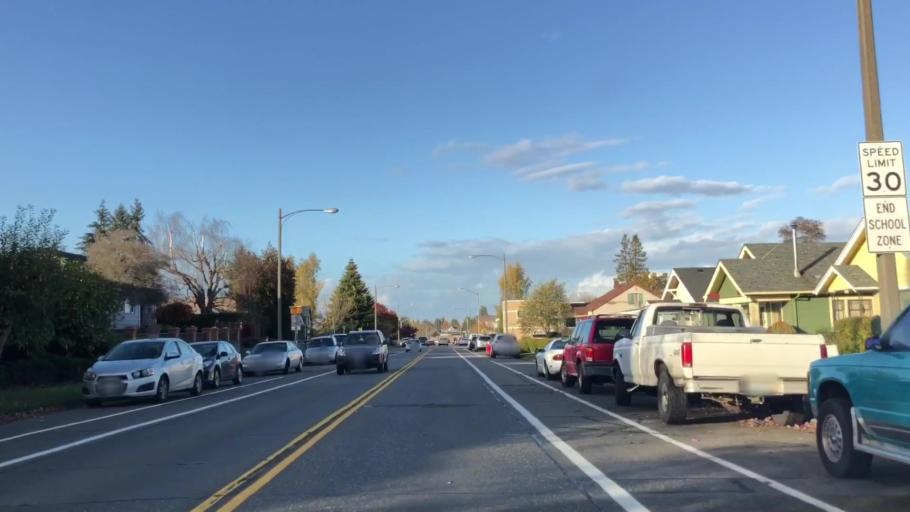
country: US
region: Washington
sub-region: Pierce County
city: Tacoma
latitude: 47.2107
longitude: -122.4432
